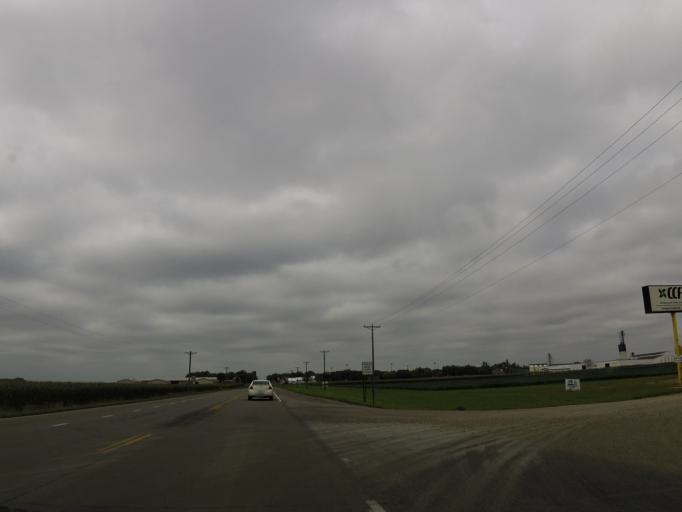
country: US
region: Minnesota
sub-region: Renville County
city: Olivia
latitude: 44.7887
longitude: -95.0869
